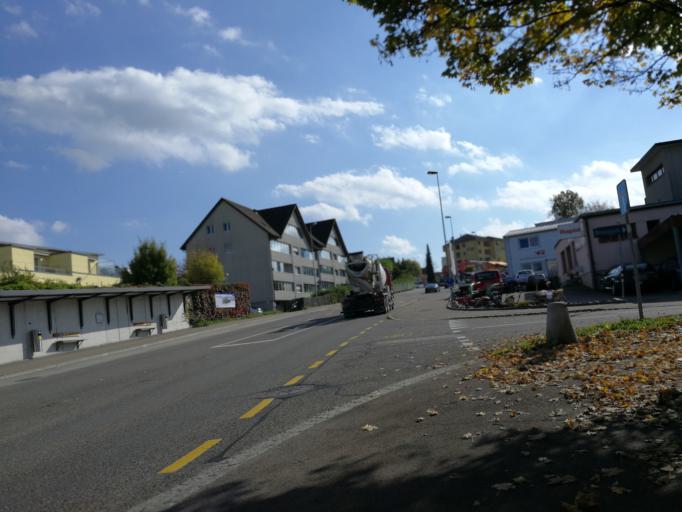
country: CH
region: Zurich
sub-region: Bezirk Meilen
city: Oetwil am See
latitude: 47.2741
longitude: 8.7196
